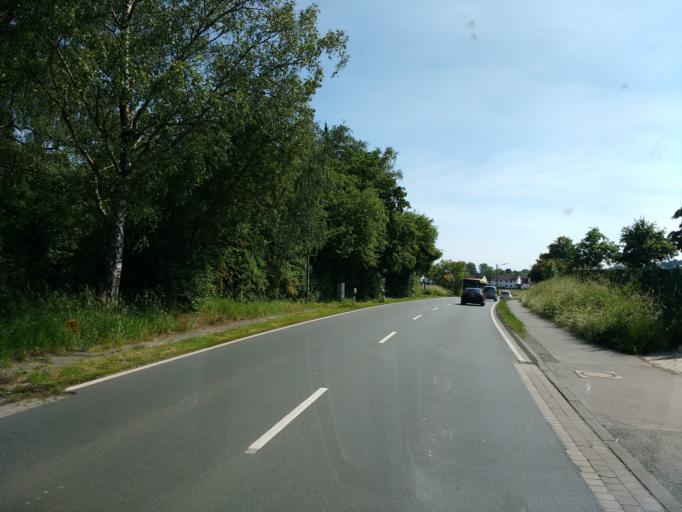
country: DE
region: North Rhine-Westphalia
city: Loehne
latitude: 52.1538
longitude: 8.6747
